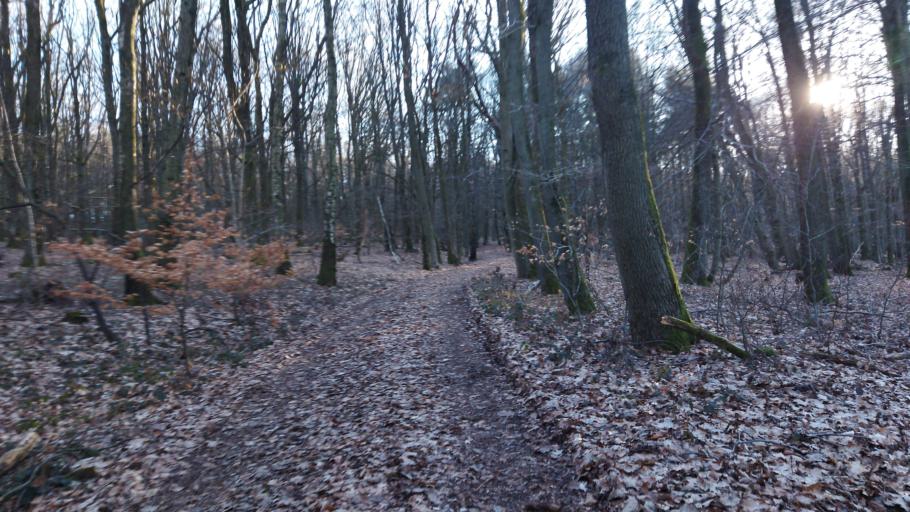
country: DE
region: Rheinland-Pfalz
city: Frohnhofen
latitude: 49.4648
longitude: 7.2923
